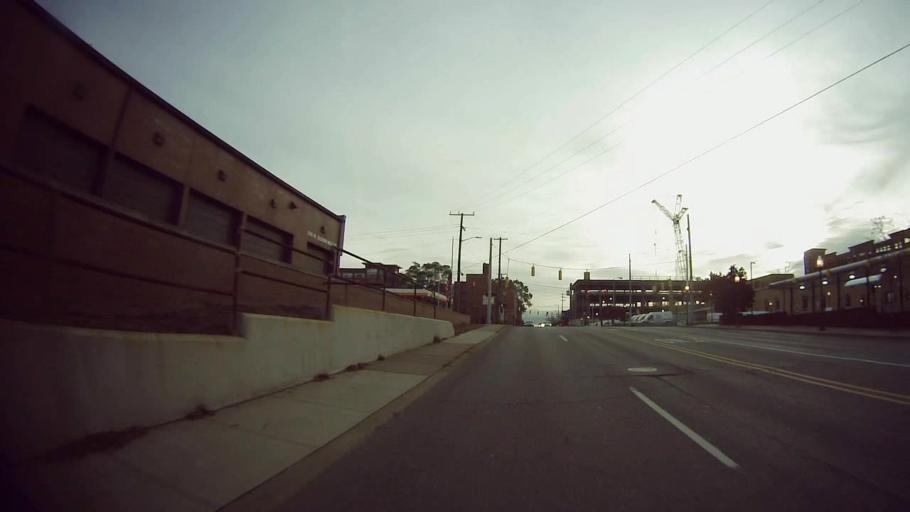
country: US
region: Michigan
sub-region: Oakland County
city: Royal Oak
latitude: 42.4898
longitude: -83.1473
